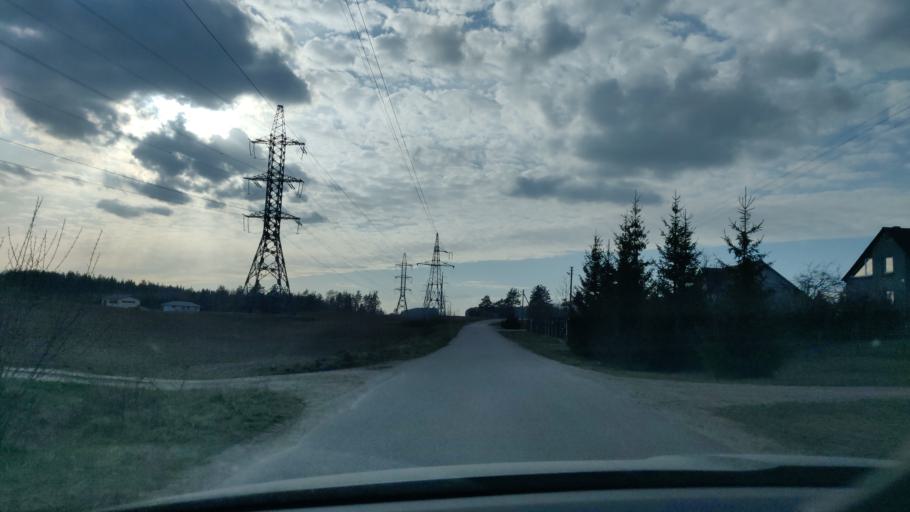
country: LT
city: Trakai
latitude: 54.6055
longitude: 24.9719
